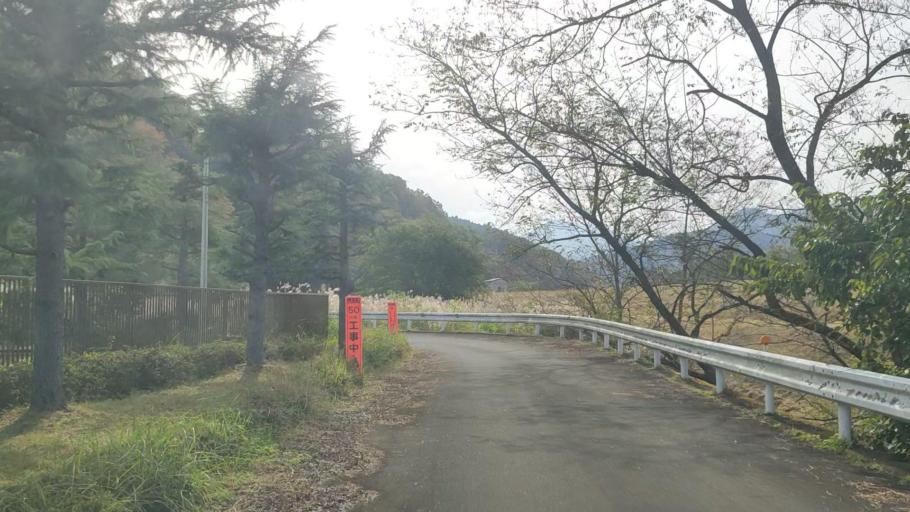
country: JP
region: Yamanashi
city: Ryuo
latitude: 35.4781
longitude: 138.4496
